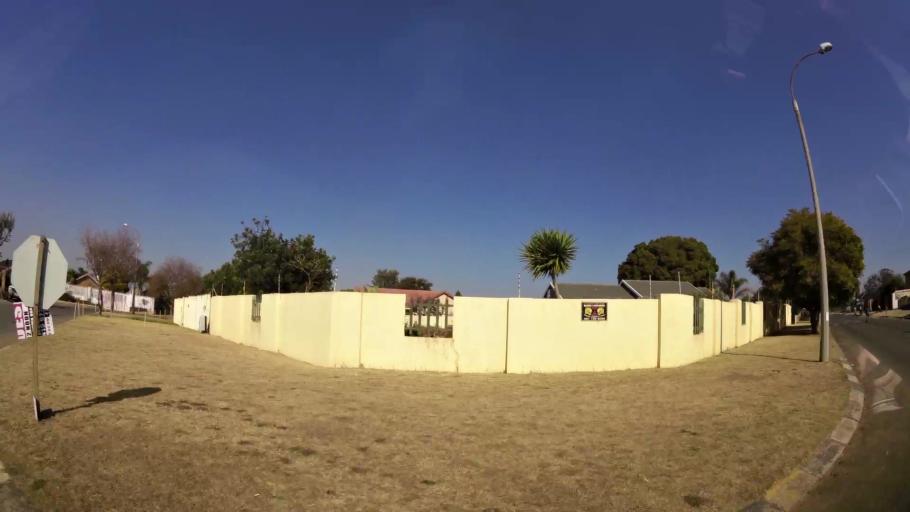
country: ZA
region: Gauteng
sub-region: West Rand District Municipality
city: Randfontein
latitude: -26.1828
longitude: 27.6792
